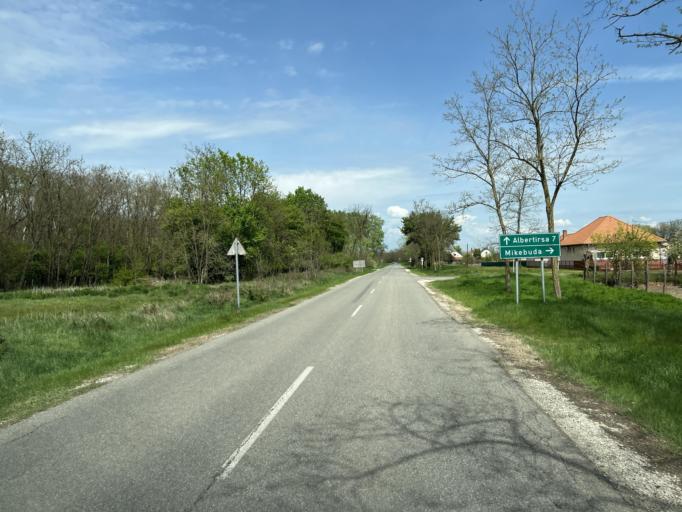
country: HU
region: Pest
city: Albertirsa
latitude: 47.1602
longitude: 19.6133
